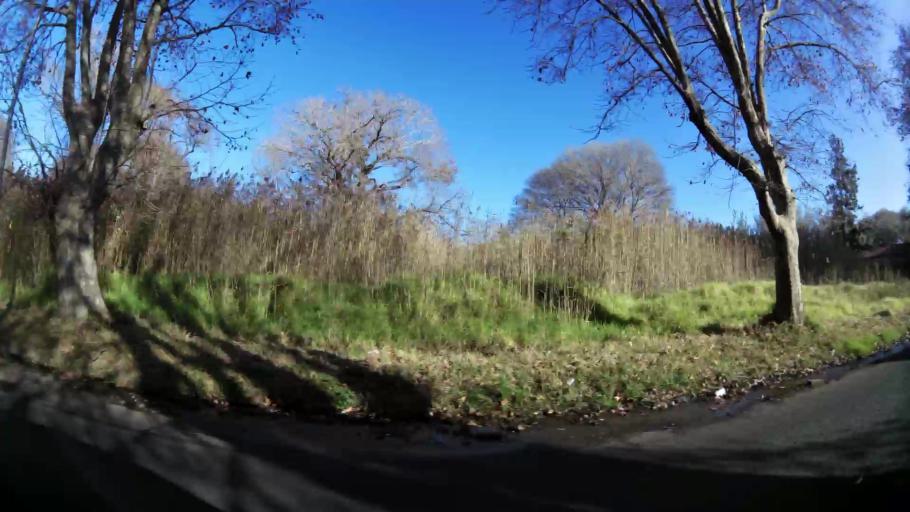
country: ZA
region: Gauteng
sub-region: City of Johannesburg Metropolitan Municipality
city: Johannesburg
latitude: -26.2039
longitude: 27.9904
